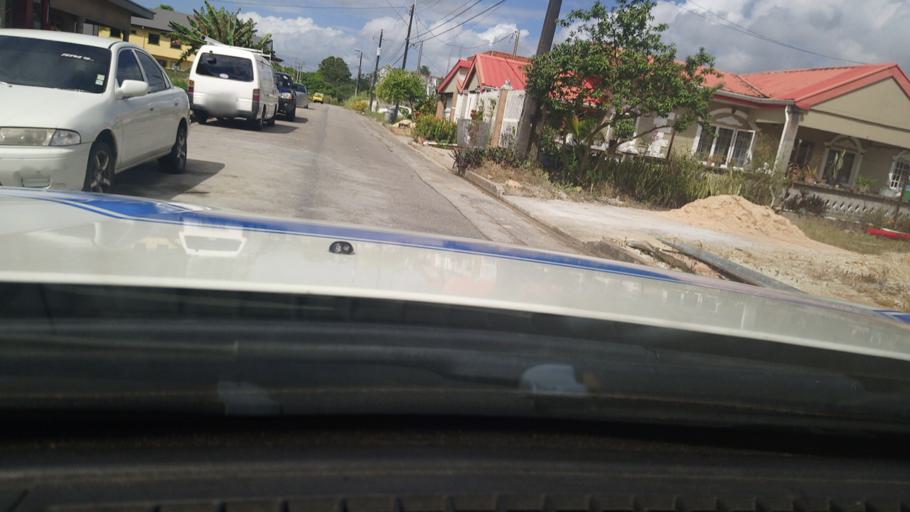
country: TT
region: Borough of Arima
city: Arima
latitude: 10.6176
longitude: -61.2984
